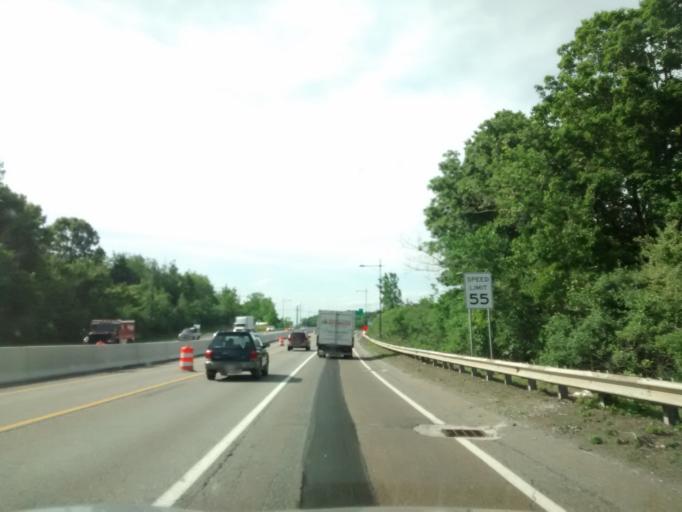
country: US
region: Massachusetts
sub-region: Worcester County
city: Millbury
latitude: 42.1969
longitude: -71.7735
